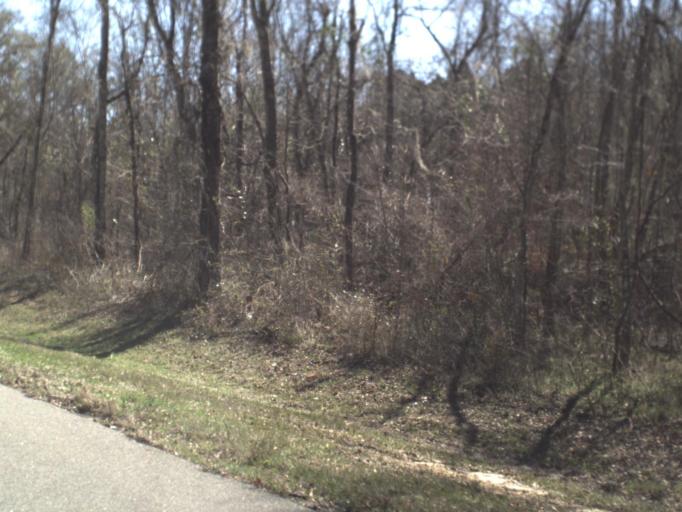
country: US
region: Florida
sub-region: Jackson County
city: Marianna
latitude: 30.8234
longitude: -85.3272
